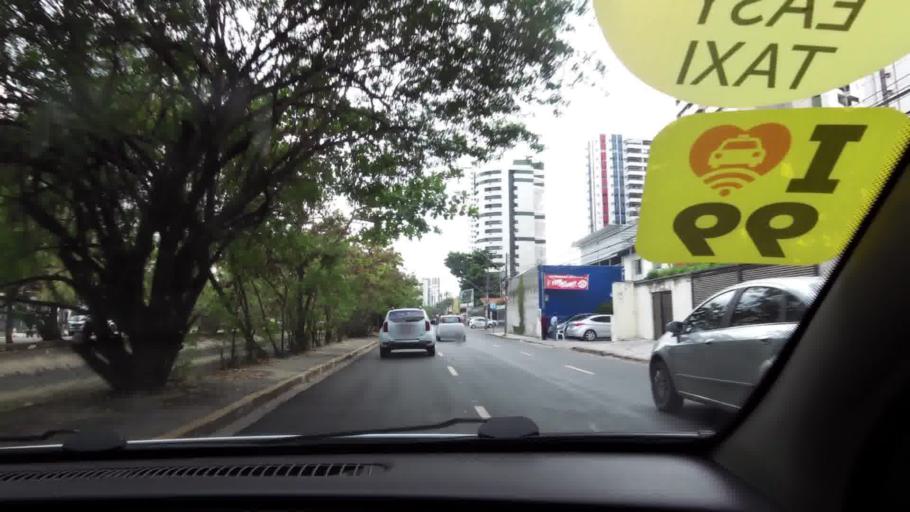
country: BR
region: Pernambuco
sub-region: Recife
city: Recife
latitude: -8.1259
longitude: -34.9018
